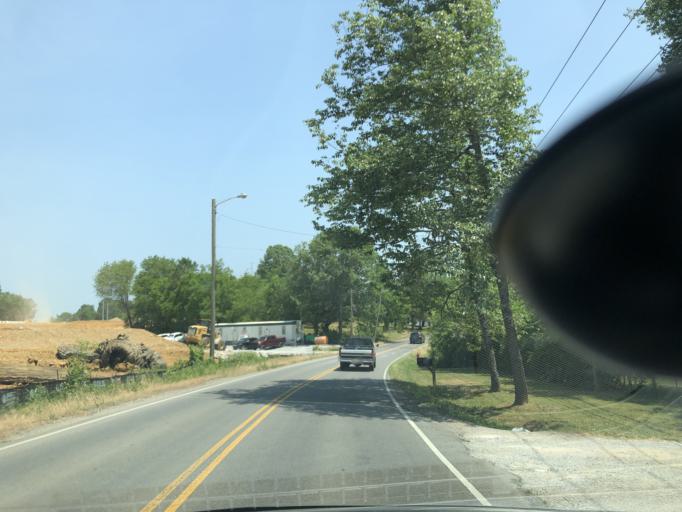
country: US
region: Tennessee
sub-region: Rutherford County
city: La Vergne
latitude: 36.0569
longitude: -86.6179
